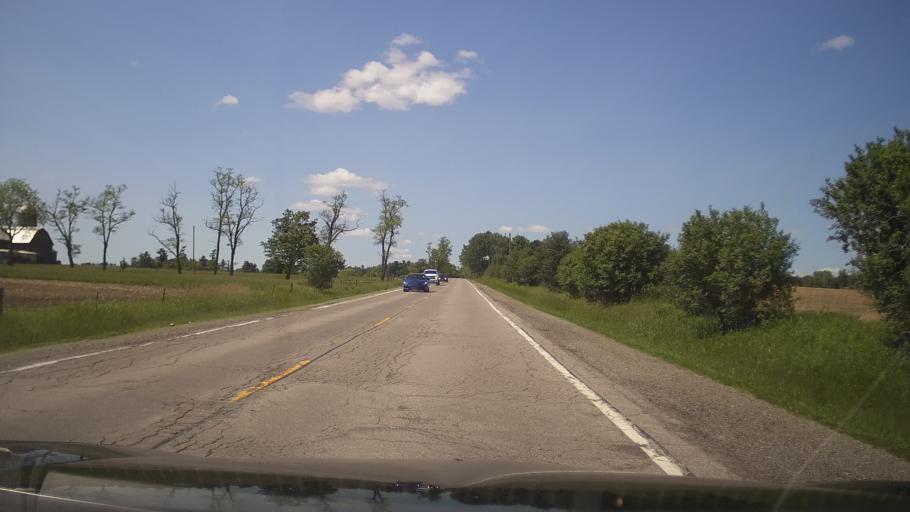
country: CA
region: Ontario
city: Oshawa
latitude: 43.9879
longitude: -78.8599
